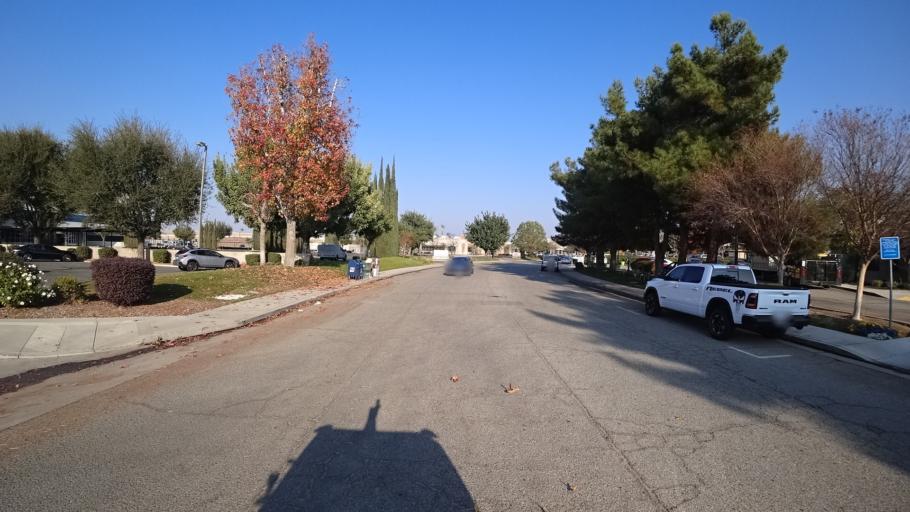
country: US
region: California
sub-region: Kern County
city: Bakersfield
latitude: 35.3674
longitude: -119.0600
